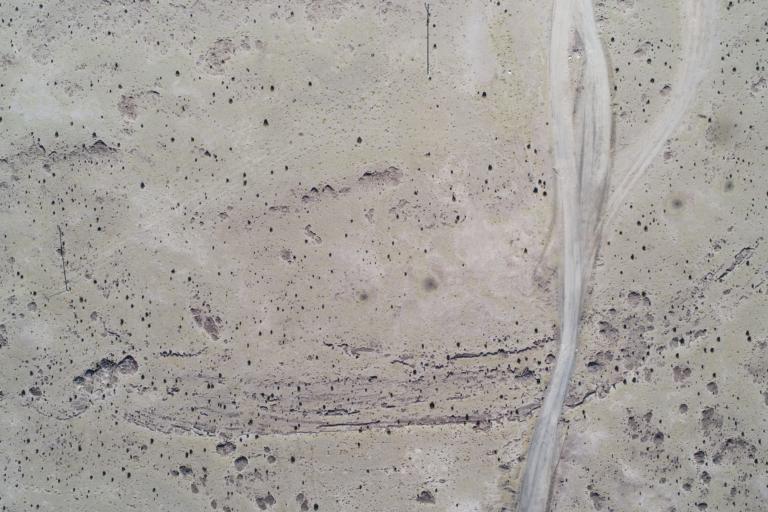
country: BO
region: Potosi
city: Colchani
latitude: -20.3521
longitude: -66.8987
